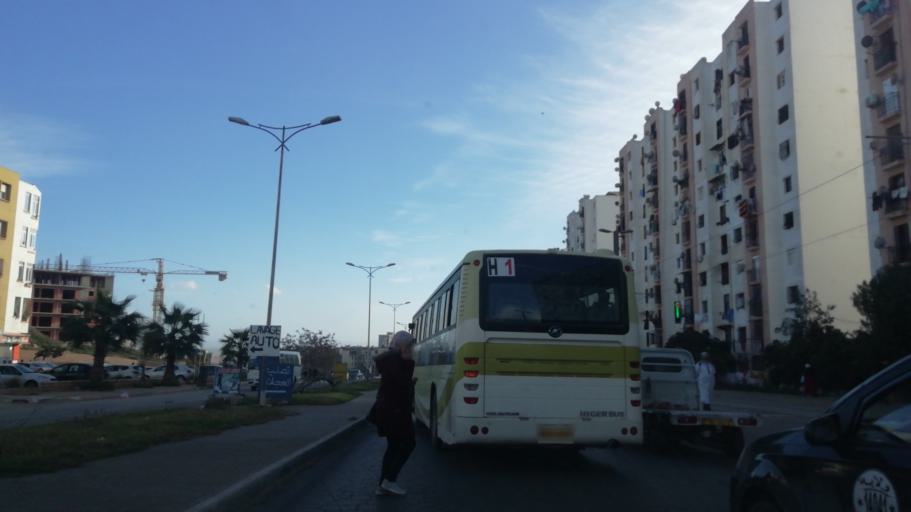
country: DZ
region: Oran
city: Bir el Djir
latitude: 35.7016
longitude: -0.5690
